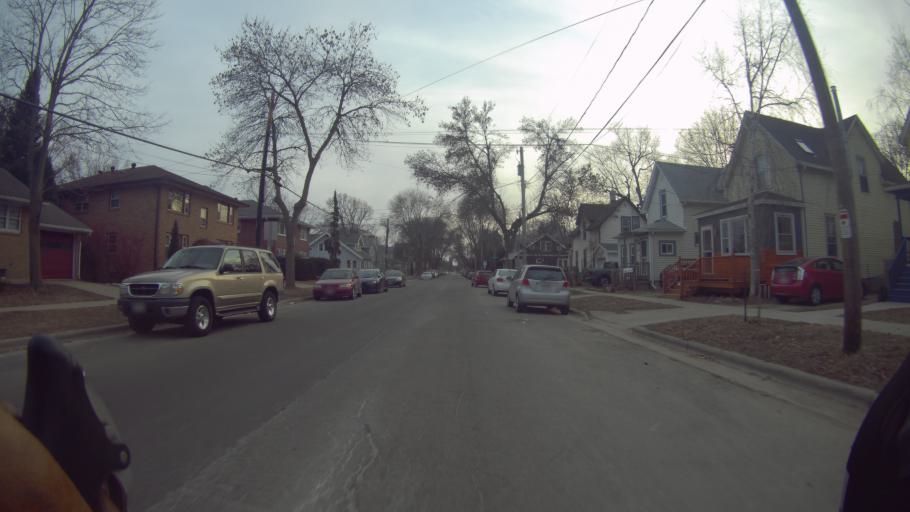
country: US
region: Wisconsin
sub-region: Dane County
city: Maple Bluff
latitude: 43.0872
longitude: -89.3686
